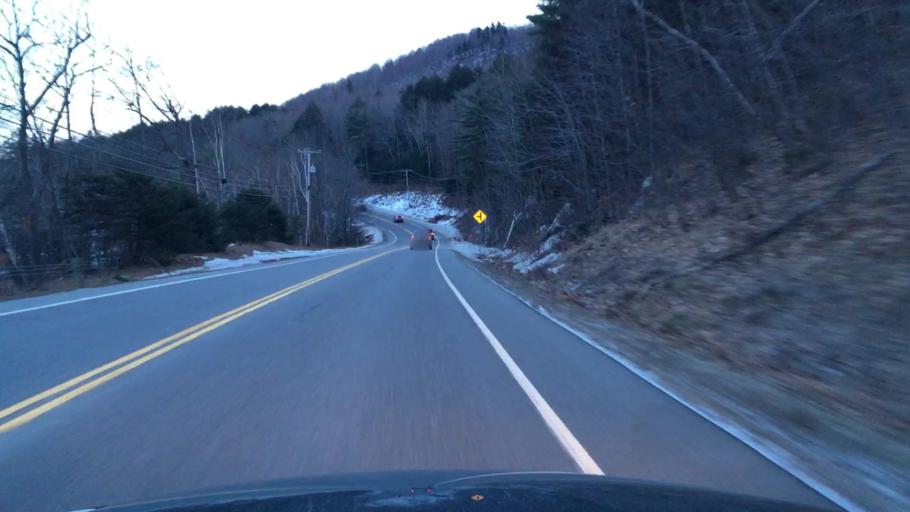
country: US
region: New Hampshire
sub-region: Merrimack County
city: Newbury
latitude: 43.3385
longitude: -72.0564
